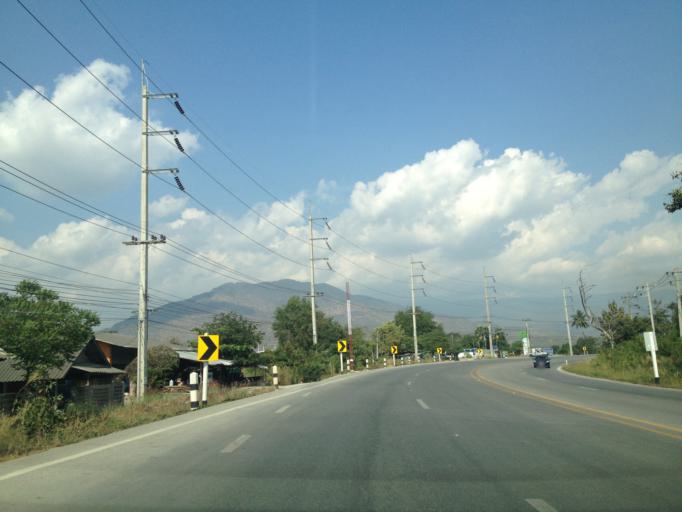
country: TH
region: Chiang Mai
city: Hot
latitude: 18.2410
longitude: 98.6048
